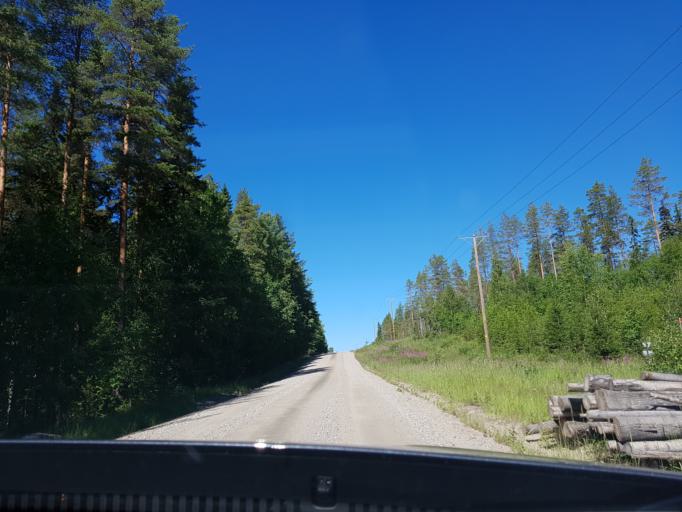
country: FI
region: Kainuu
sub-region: Kehys-Kainuu
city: Kuhmo
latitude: 64.1696
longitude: 29.6453
